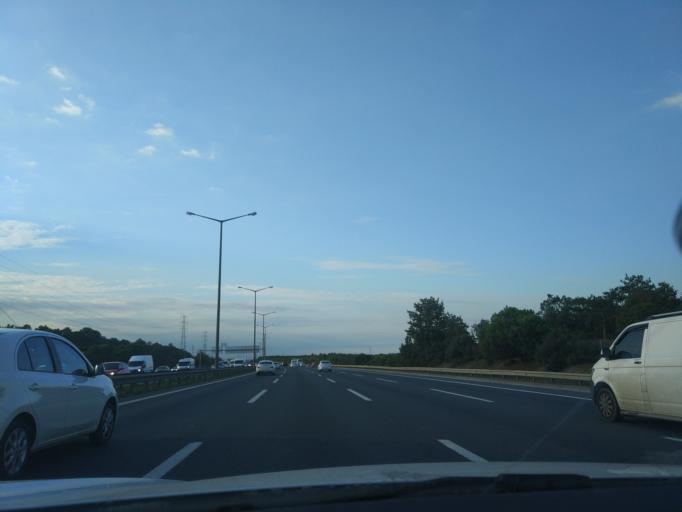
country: TR
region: Istanbul
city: Umraniye
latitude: 41.0595
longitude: 29.1171
